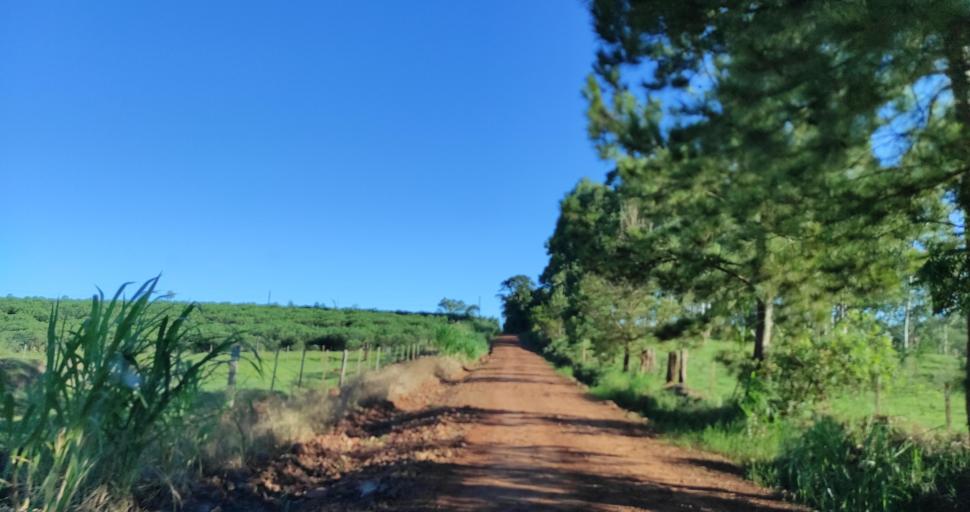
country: AR
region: Misiones
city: Puerto Rico
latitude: -26.8509
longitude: -55.0137
